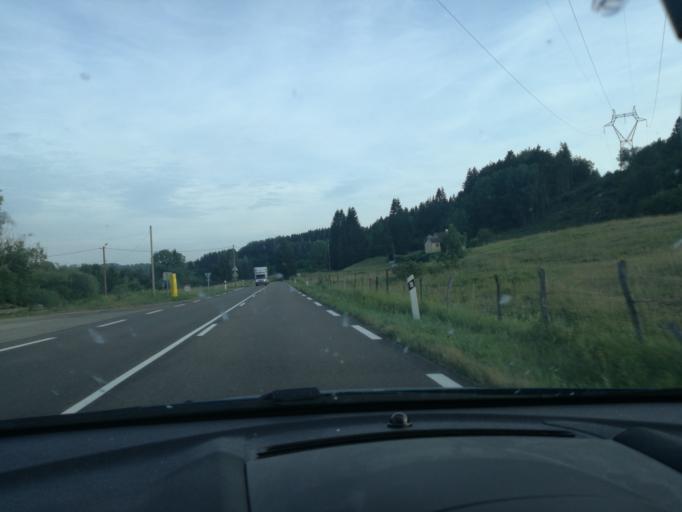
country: FR
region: Franche-Comte
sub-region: Departement du Jura
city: Morbier
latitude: 46.6164
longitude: 5.9591
